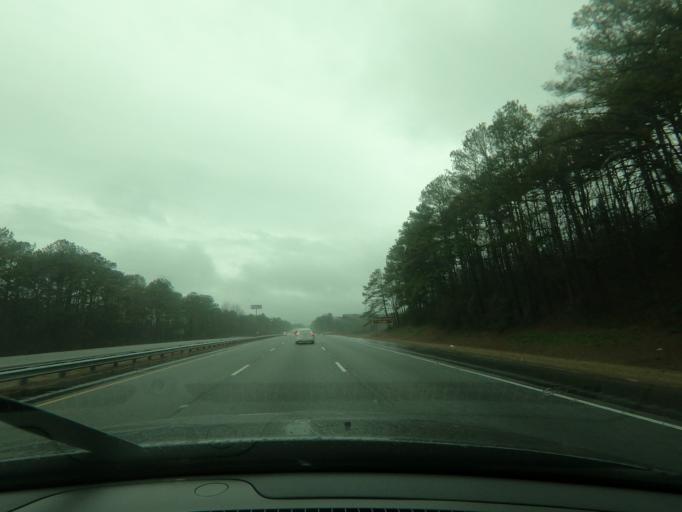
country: US
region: Georgia
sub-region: Bartow County
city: Adairsville
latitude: 34.3656
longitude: -84.8997
